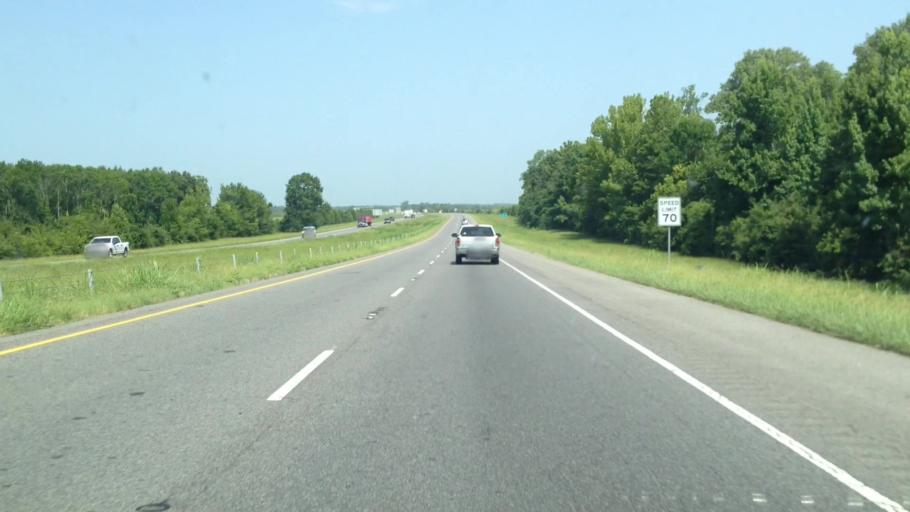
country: US
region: Louisiana
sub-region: Madison Parish
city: Tallulah
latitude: 32.3977
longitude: -91.2091
